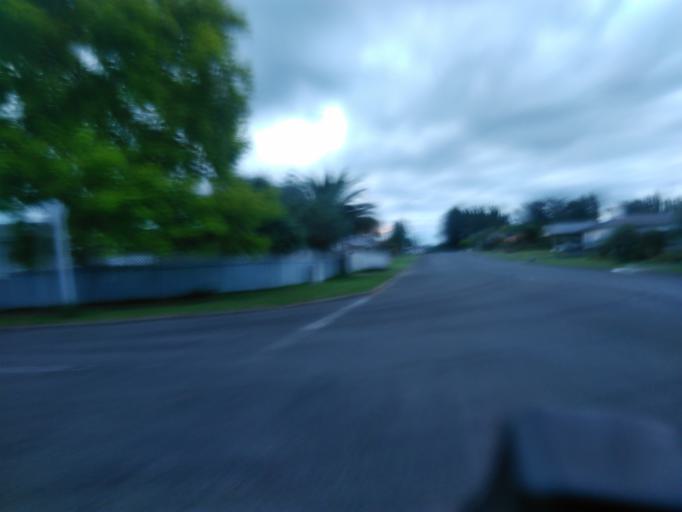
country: NZ
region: Gisborne
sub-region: Gisborne District
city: Gisborne
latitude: -38.6449
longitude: 177.9900
